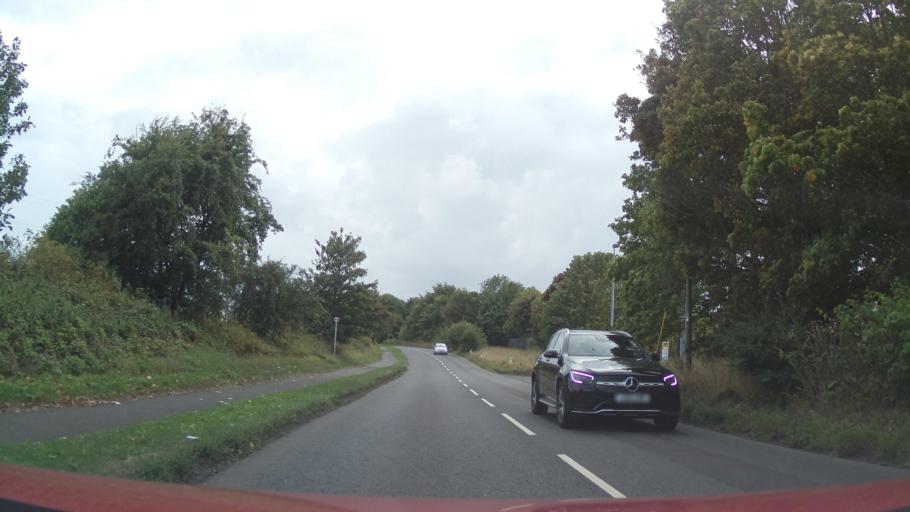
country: GB
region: Scotland
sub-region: East Lothian
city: Cockenzie
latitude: 55.9640
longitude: -2.9579
